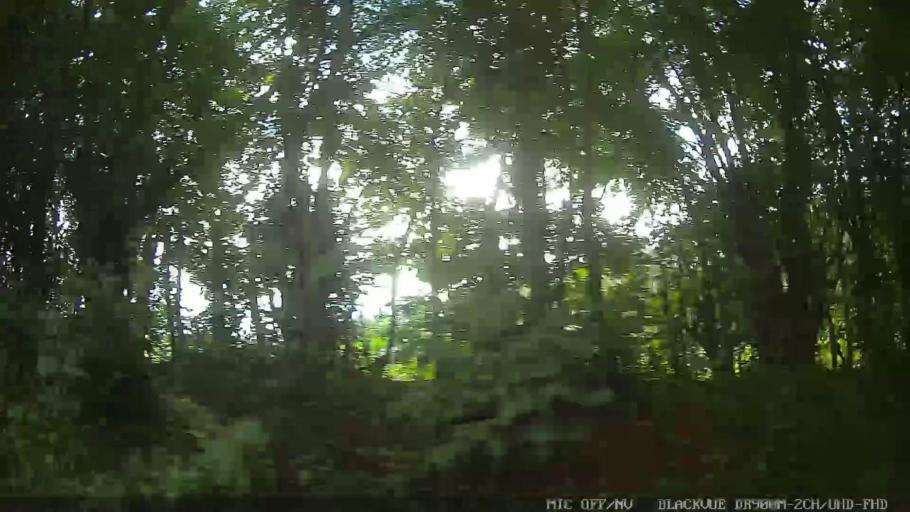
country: BR
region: Sao Paulo
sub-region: Braganca Paulista
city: Braganca Paulista
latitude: -23.0336
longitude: -46.4803
